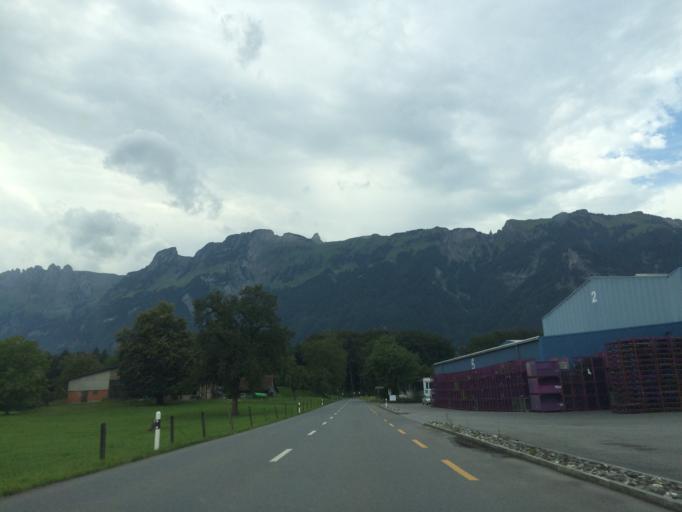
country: LI
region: Ruggell
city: Ruggell
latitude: 47.2444
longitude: 9.5123
